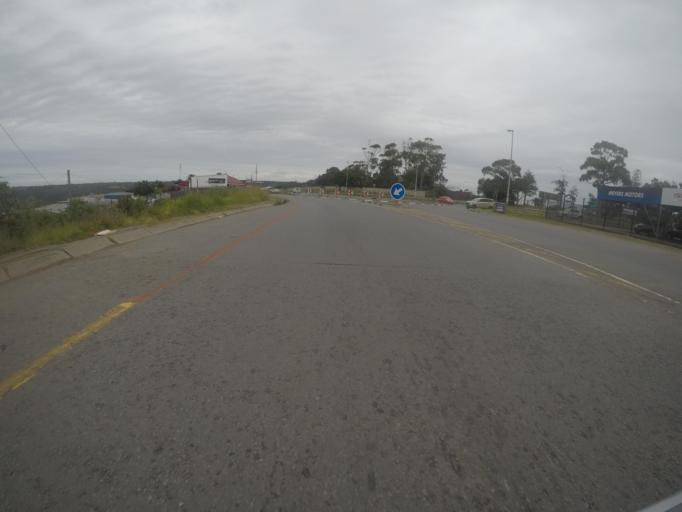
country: ZA
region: Eastern Cape
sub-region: Buffalo City Metropolitan Municipality
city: East London
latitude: -32.9496
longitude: 27.9206
